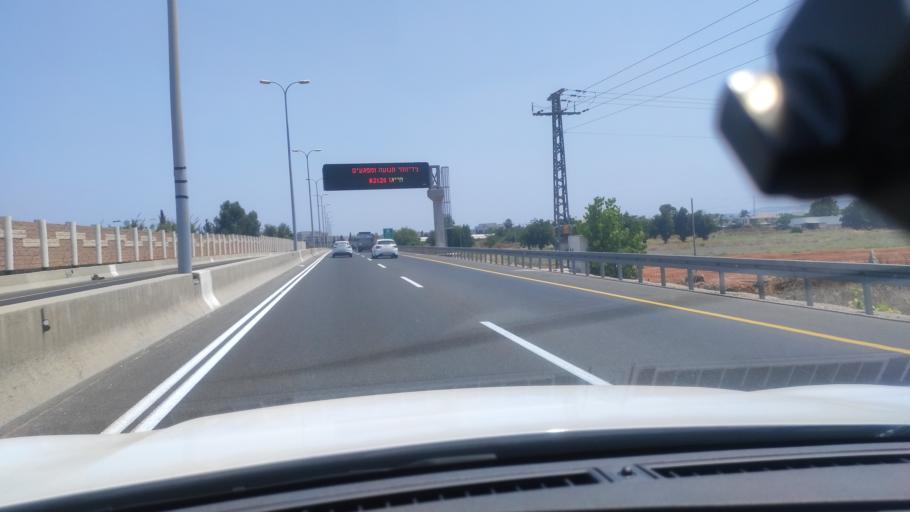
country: IL
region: Central District
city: Kfar Saba
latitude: 32.1546
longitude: 34.9238
